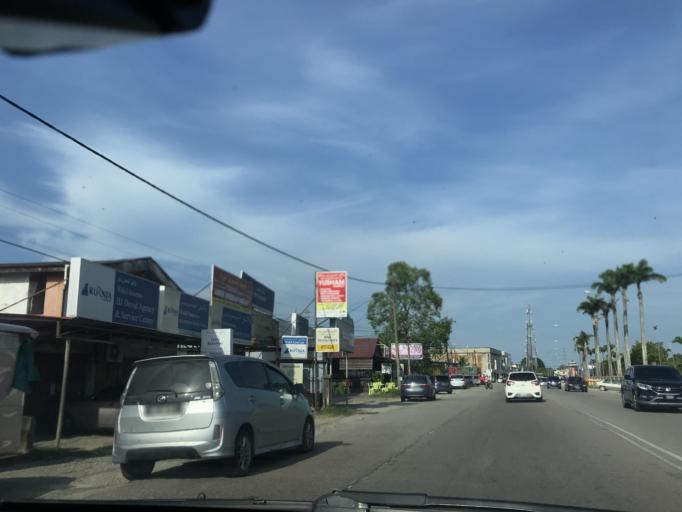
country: MY
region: Kelantan
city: Kota Bharu
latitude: 6.1193
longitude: 102.2898
